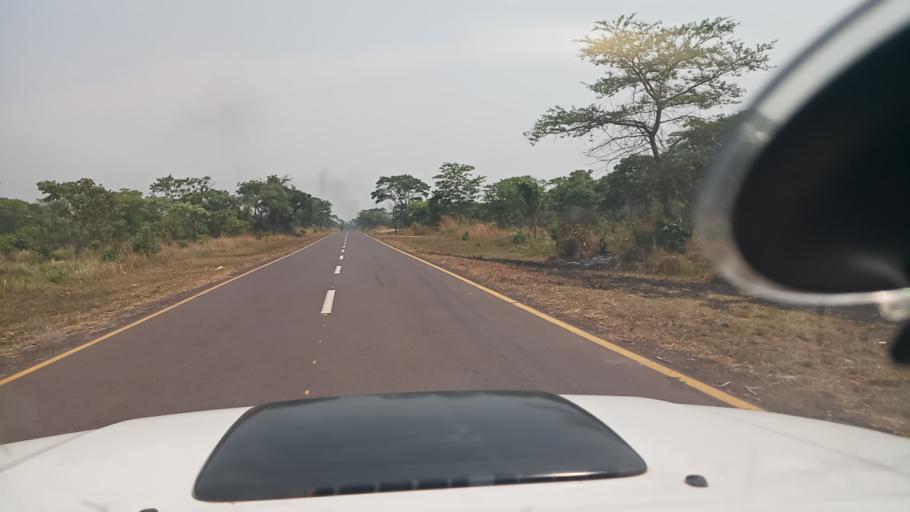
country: ZM
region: Luapula
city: Mwense
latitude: -10.8019
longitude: 28.2325
